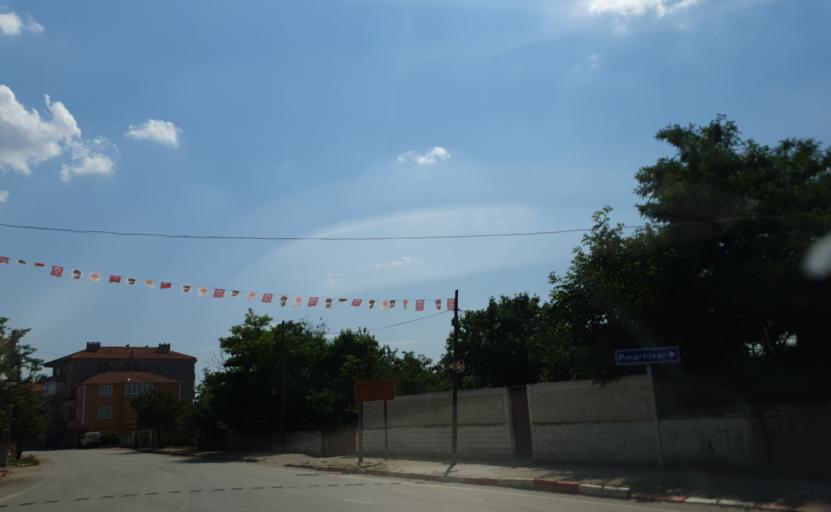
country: TR
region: Kirklareli
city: Buyukkaristiran
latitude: 41.4429
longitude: 27.5871
